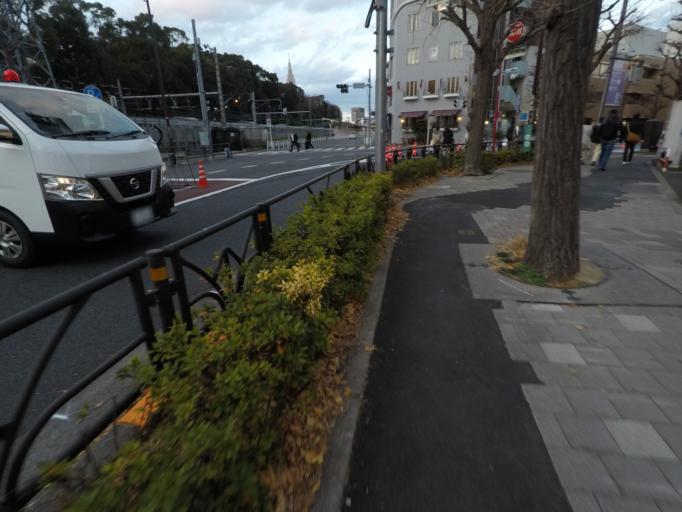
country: JP
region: Tokyo
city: Tokyo
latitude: 35.6726
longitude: 139.7034
